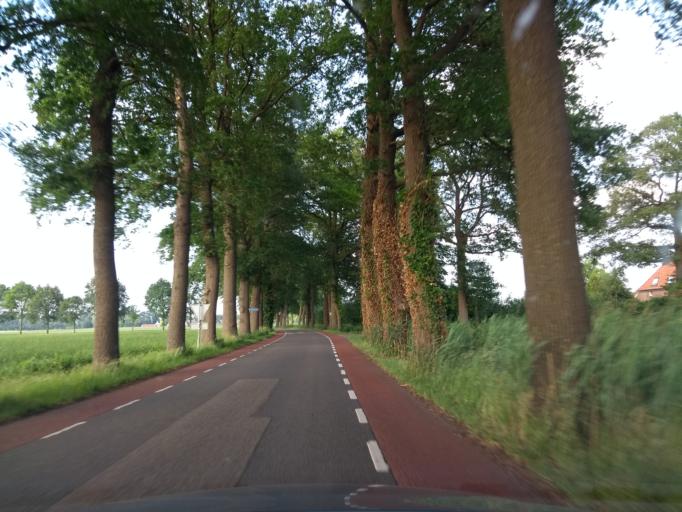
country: NL
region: Gelderland
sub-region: Berkelland
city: Borculo
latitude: 52.1347
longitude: 6.5169
